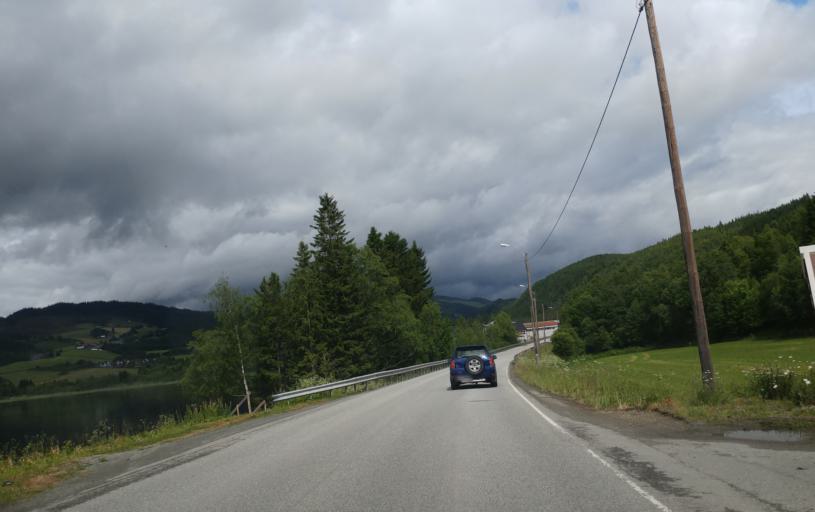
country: NO
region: Sor-Trondelag
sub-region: Selbu
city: Mebonden
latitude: 63.2739
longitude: 11.0774
